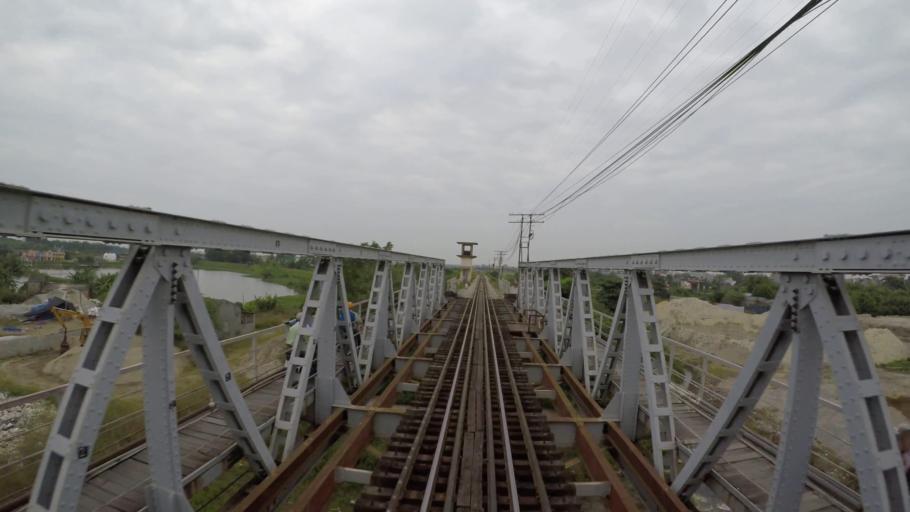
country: VN
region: Hai Duong
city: Thanh Pho Hai Duong
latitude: 20.9564
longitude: 106.3655
